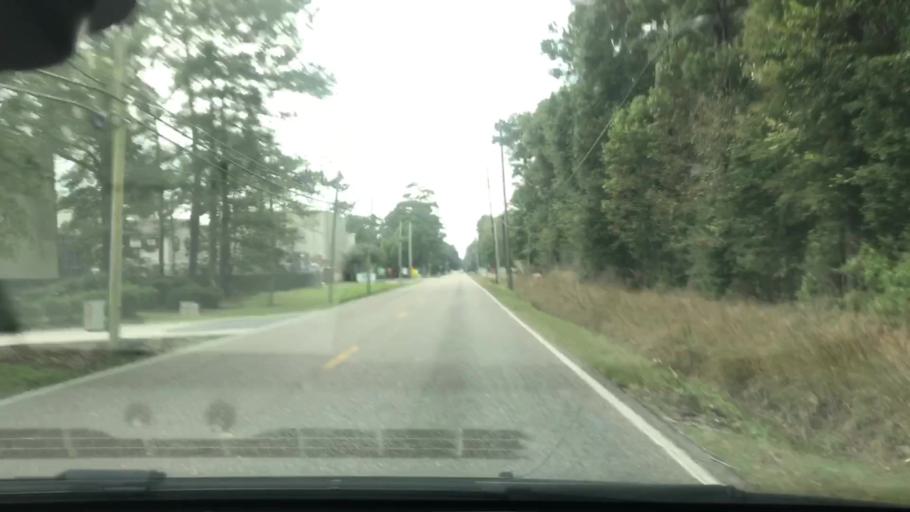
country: US
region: Louisiana
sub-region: Saint Tammany Parish
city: Abita Springs
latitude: 30.4827
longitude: -90.0544
